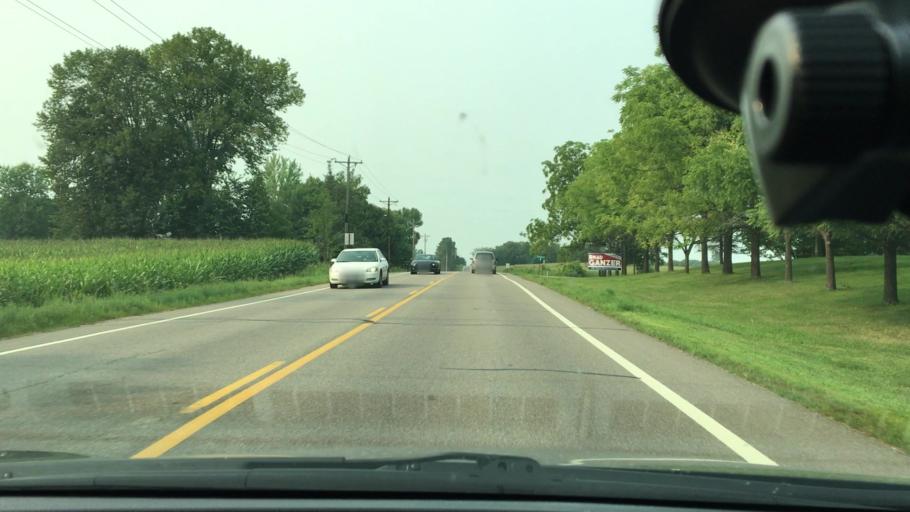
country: US
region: Minnesota
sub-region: Hennepin County
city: Champlin
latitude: 45.1729
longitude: -93.4623
